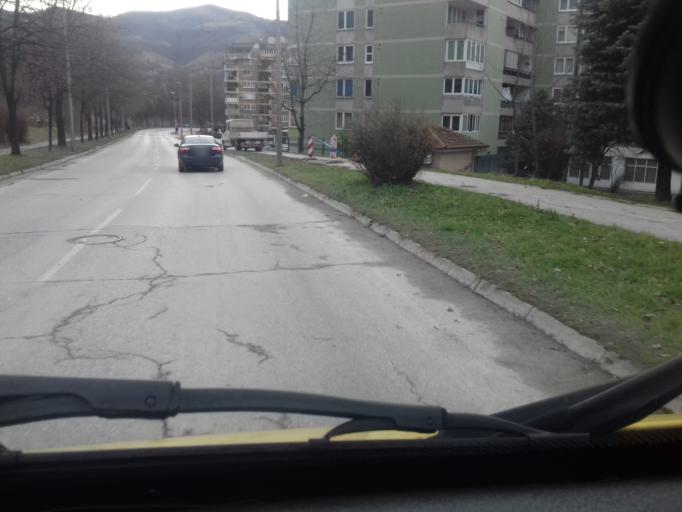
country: BA
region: Federation of Bosnia and Herzegovina
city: Zenica
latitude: 44.2005
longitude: 17.9259
